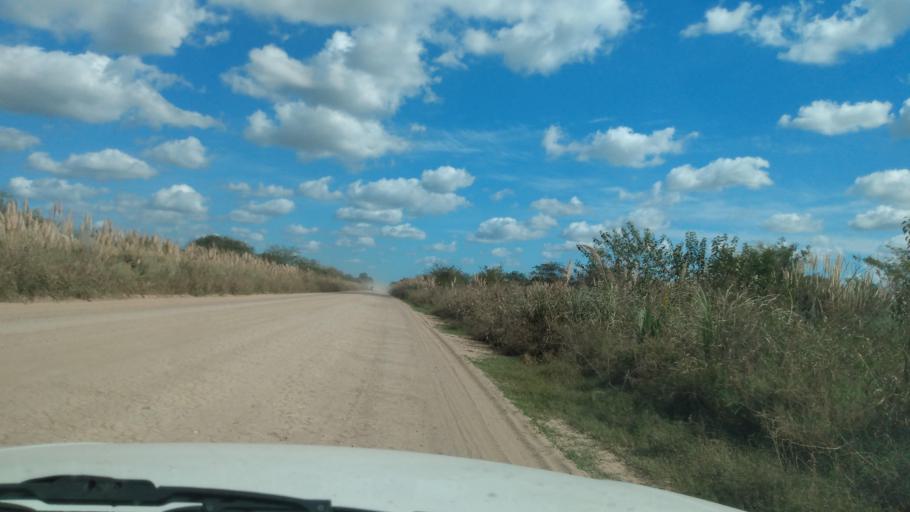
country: AR
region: Buenos Aires
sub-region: Partido de Navarro
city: Navarro
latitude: -34.9986
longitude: -59.3263
